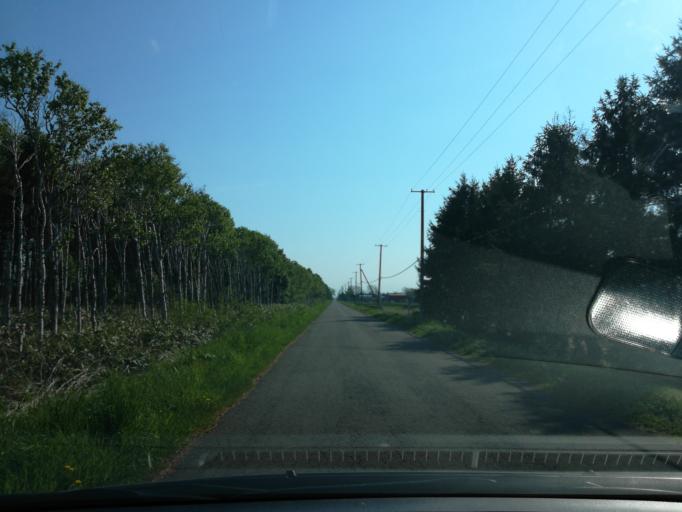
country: JP
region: Hokkaido
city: Ebetsu
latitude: 43.1180
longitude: 141.6508
